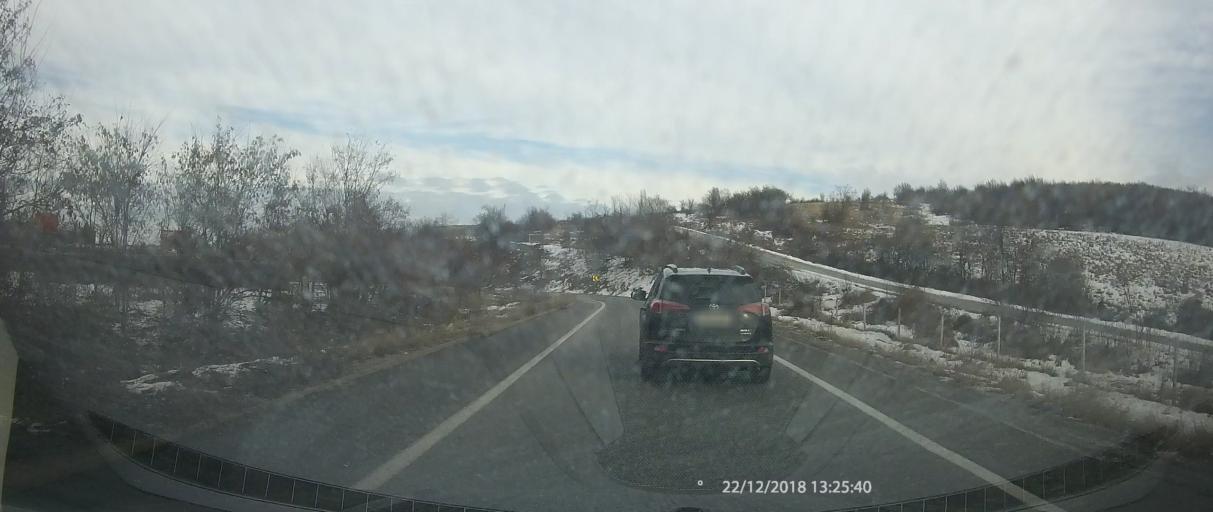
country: BG
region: Lovech
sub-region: Obshtina Yablanitsa
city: Yablanitsa
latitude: 43.0369
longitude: 24.1204
